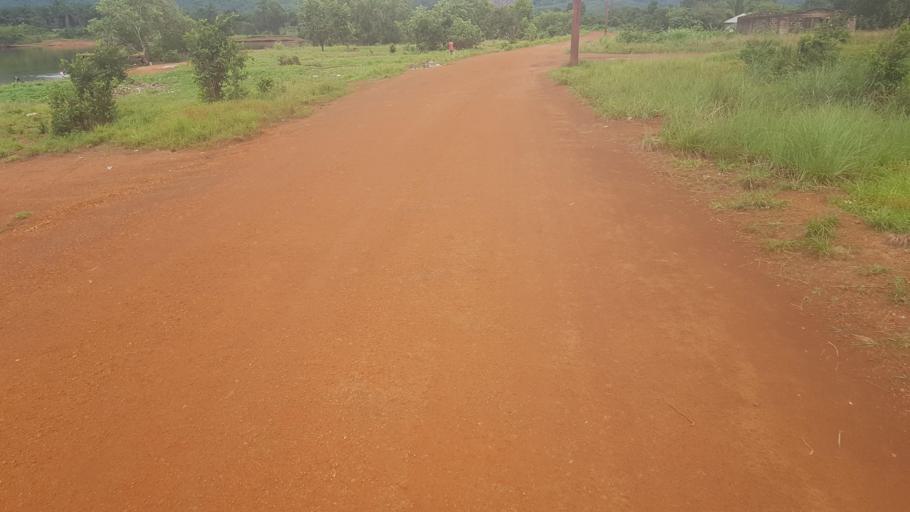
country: SL
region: Southern Province
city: Mogbwemo
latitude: 7.7562
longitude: -12.3053
